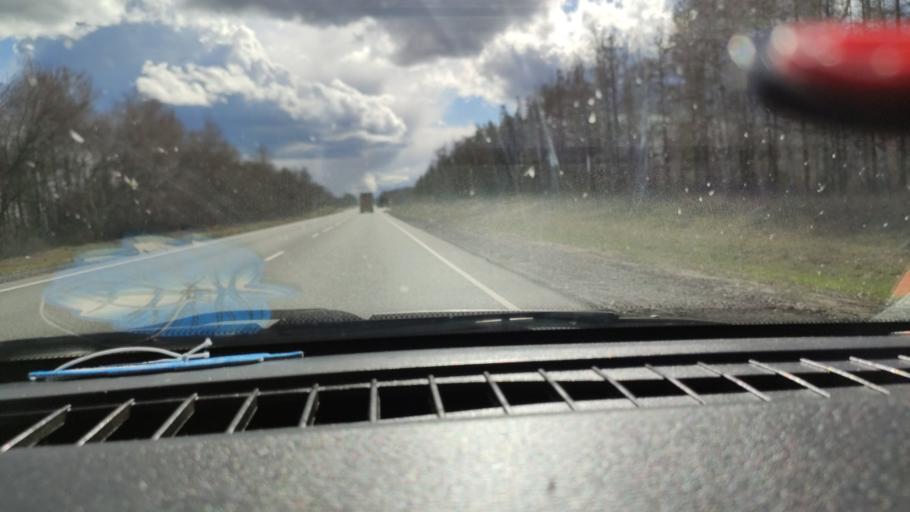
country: RU
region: Saratov
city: Khvalynsk
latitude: 52.5669
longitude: 48.0967
